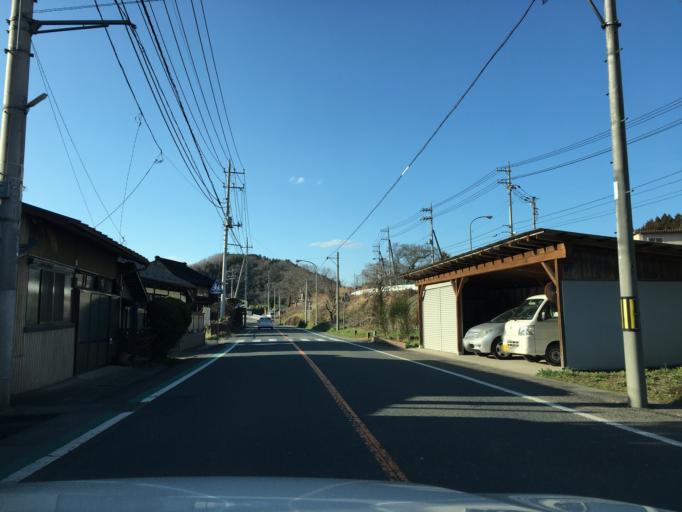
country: JP
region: Ibaraki
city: Daigo
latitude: 36.7765
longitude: 140.3464
